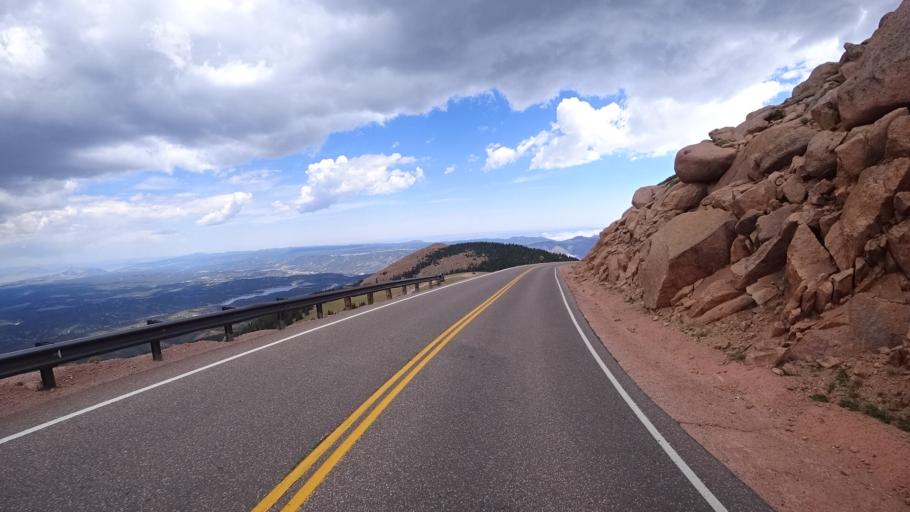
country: US
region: Colorado
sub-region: El Paso County
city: Cascade-Chipita Park
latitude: 38.8744
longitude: -105.0676
